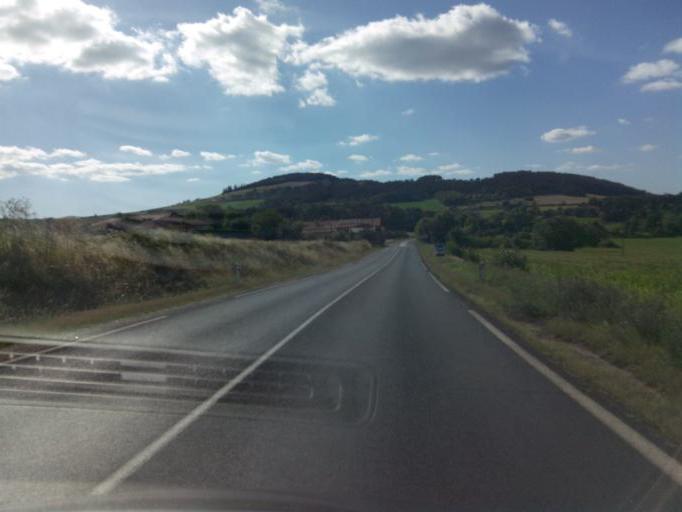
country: FR
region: Auvergne
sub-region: Departement de la Haute-Loire
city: Polignac
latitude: 45.0810
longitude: 3.8251
